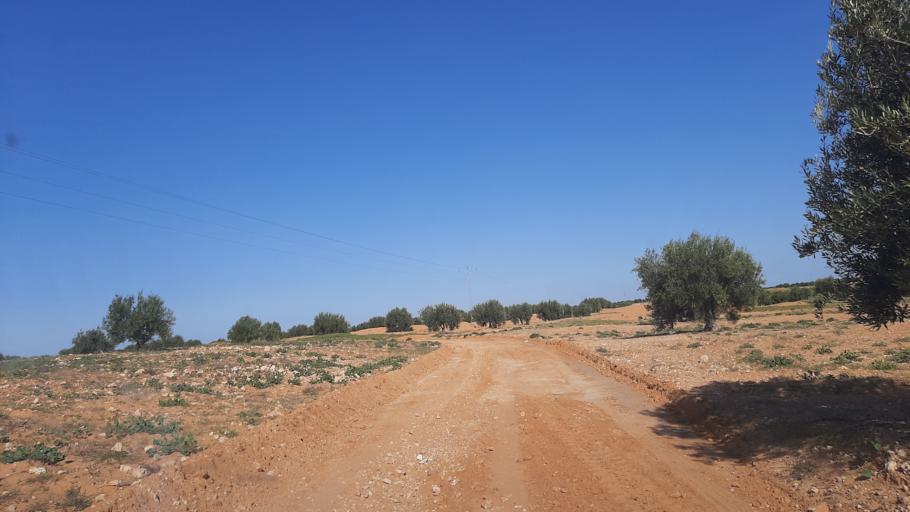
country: TN
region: Madanin
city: Medenine
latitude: 33.2820
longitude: 10.7829
